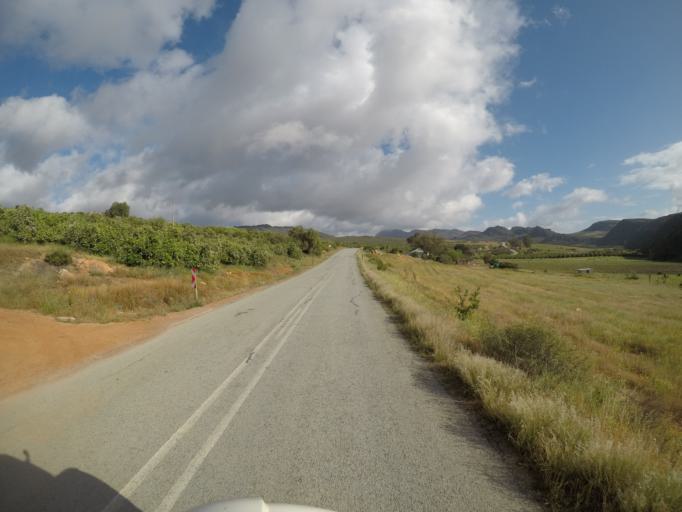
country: ZA
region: Western Cape
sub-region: West Coast District Municipality
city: Clanwilliam
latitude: -32.4377
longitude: 18.9409
